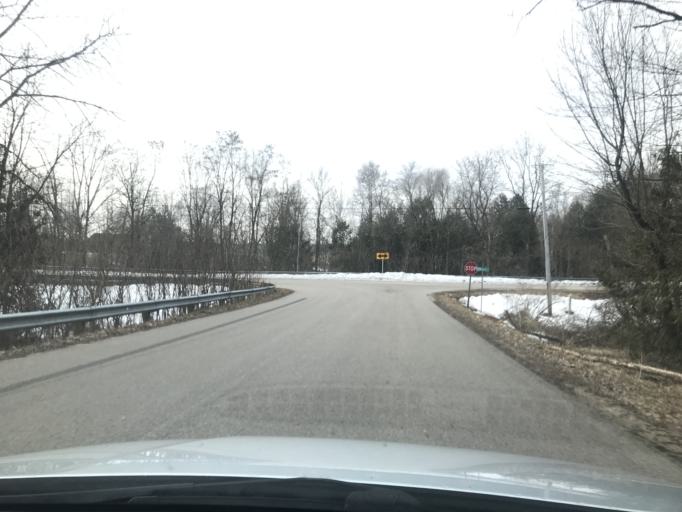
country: US
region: Wisconsin
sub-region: Oconto County
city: Oconto Falls
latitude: 44.8508
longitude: -88.1472
